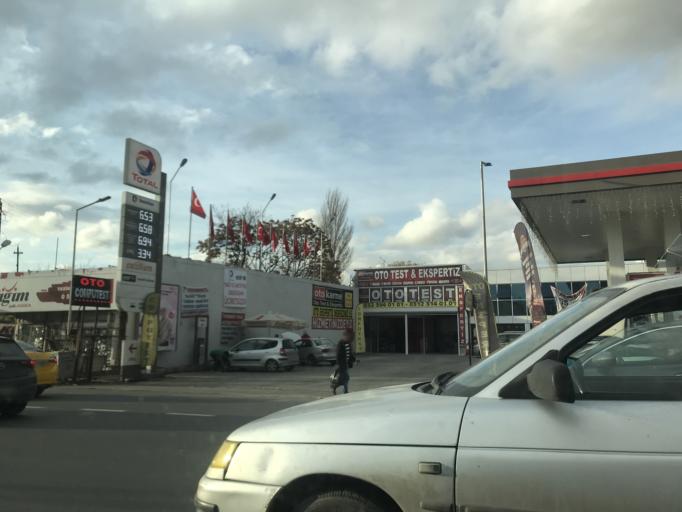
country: TR
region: Ankara
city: Ankara
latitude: 39.9564
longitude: 32.8456
